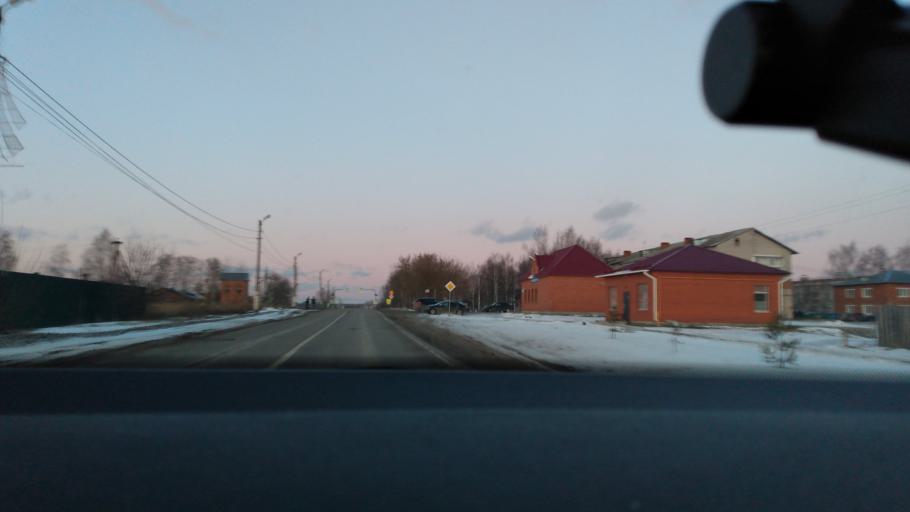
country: RU
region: Moskovskaya
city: Krasnaya Poyma
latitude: 55.1185
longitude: 39.0718
